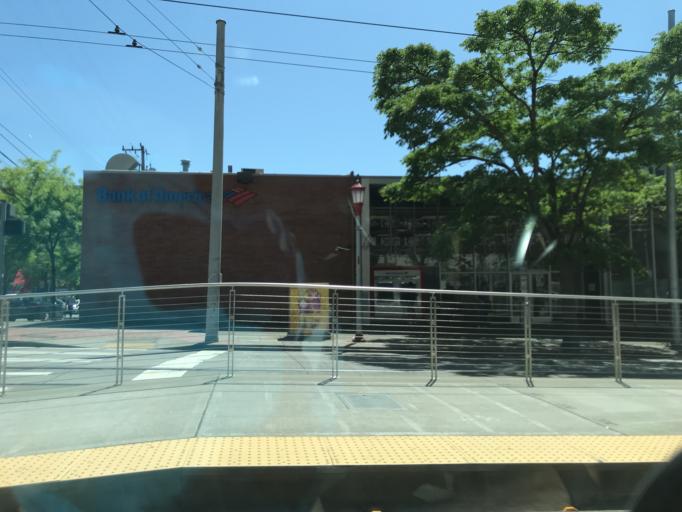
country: US
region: Washington
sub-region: King County
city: Seattle
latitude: 47.5992
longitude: -122.3263
